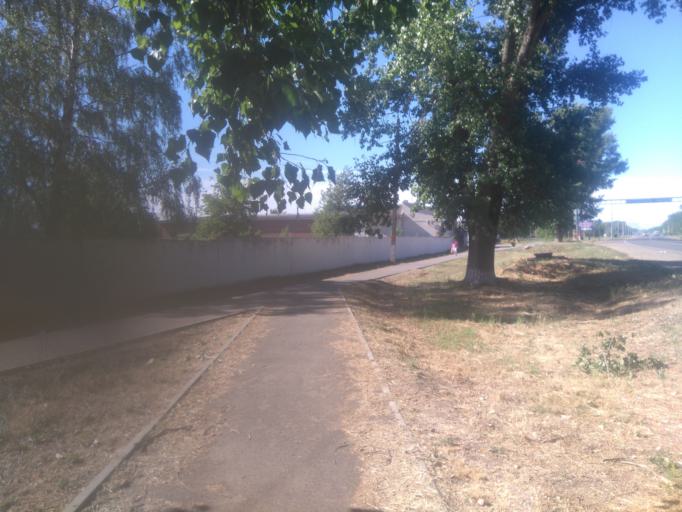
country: RU
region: Krasnodarskiy
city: Fastovetskaya
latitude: 45.9098
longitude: 40.1518
